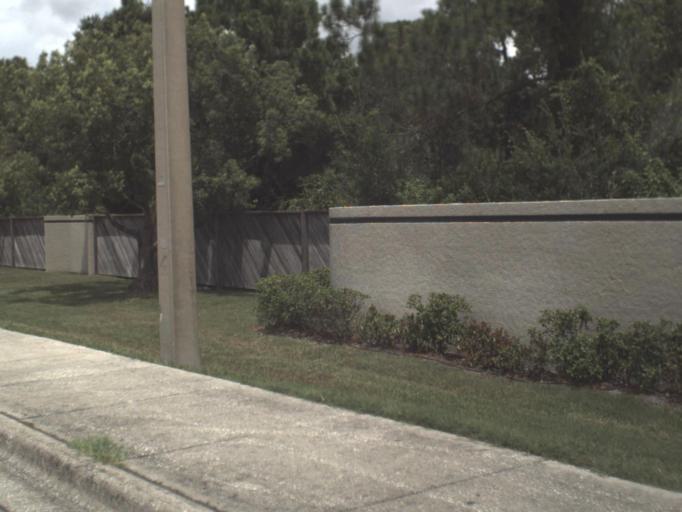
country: US
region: Florida
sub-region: Pinellas County
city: Oldsmar
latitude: 28.0481
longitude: -82.6911
